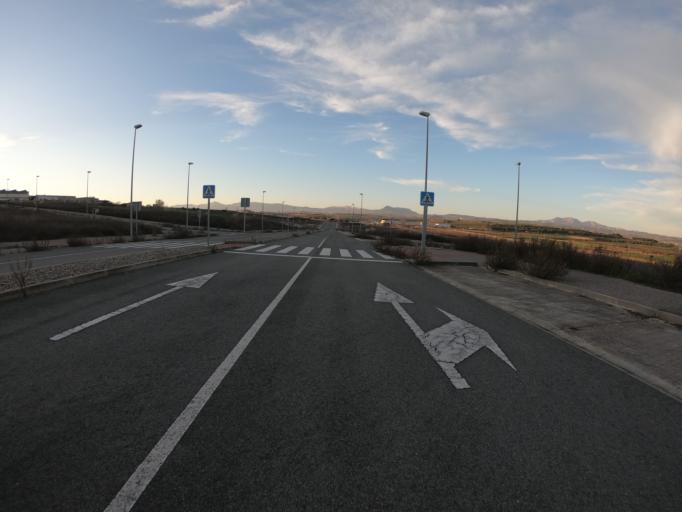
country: ES
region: Basque Country
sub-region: Provincia de Alava
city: Oyon
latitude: 42.4819
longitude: -2.4134
